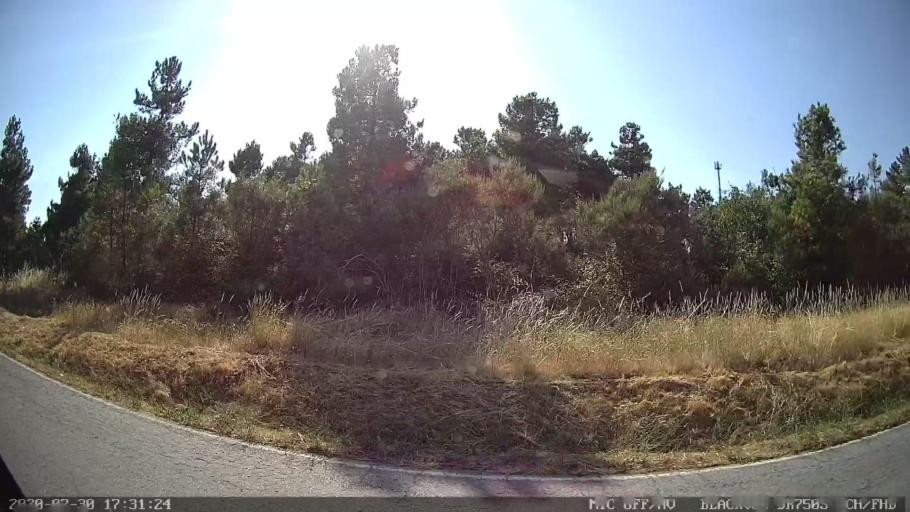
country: PT
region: Vila Real
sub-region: Murca
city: Murca
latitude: 41.3430
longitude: -7.4729
